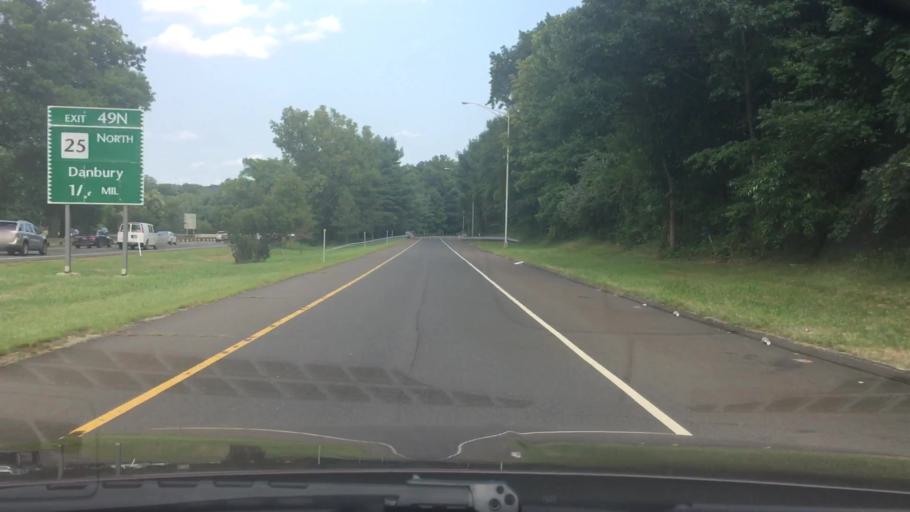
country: US
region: Connecticut
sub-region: Fairfield County
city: Trumbull
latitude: 41.2343
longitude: -73.1979
